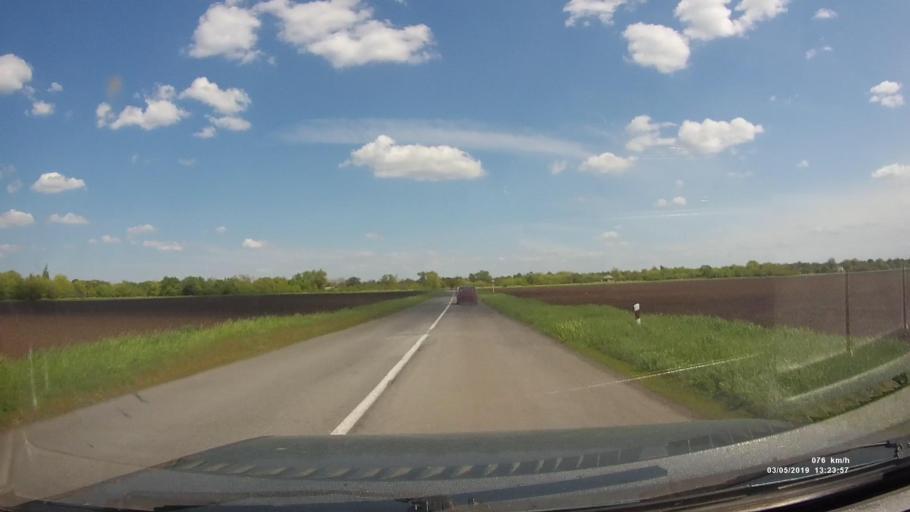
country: RU
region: Rostov
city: Semikarakorsk
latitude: 47.5625
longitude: 40.7888
